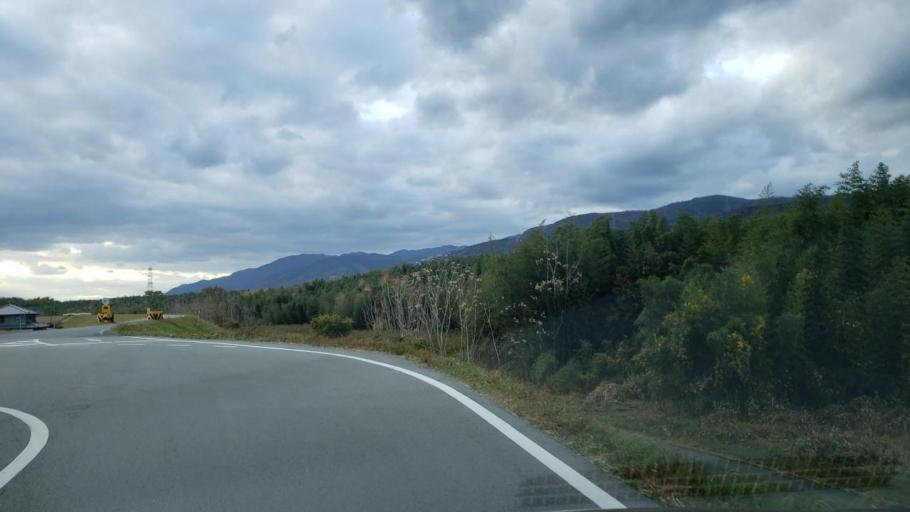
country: JP
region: Tokushima
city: Wakimachi
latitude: 34.0626
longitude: 134.1427
